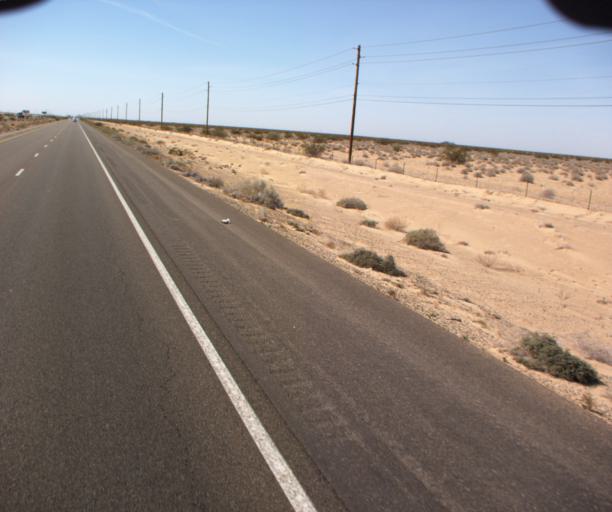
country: MX
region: Sonora
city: San Luis Rio Colorado
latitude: 32.4948
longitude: -114.6778
